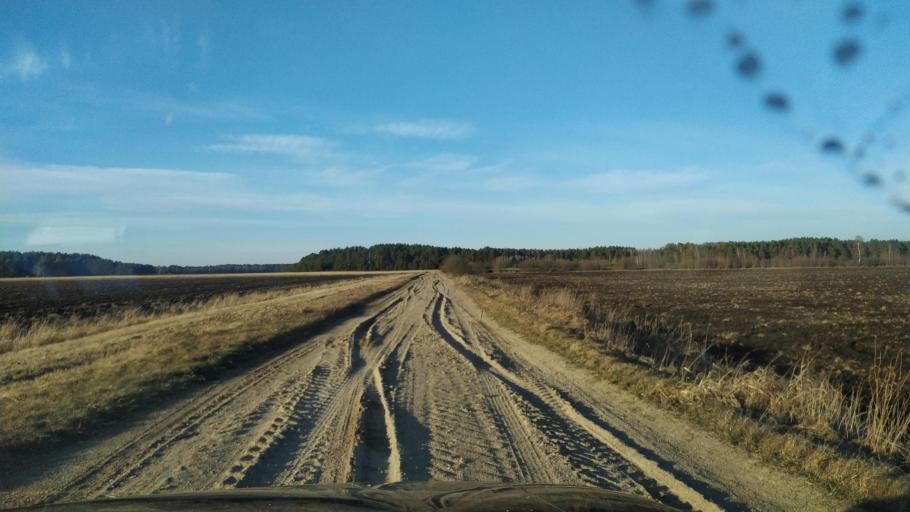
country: BY
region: Brest
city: Pruzhany
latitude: 52.5502
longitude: 24.3030
